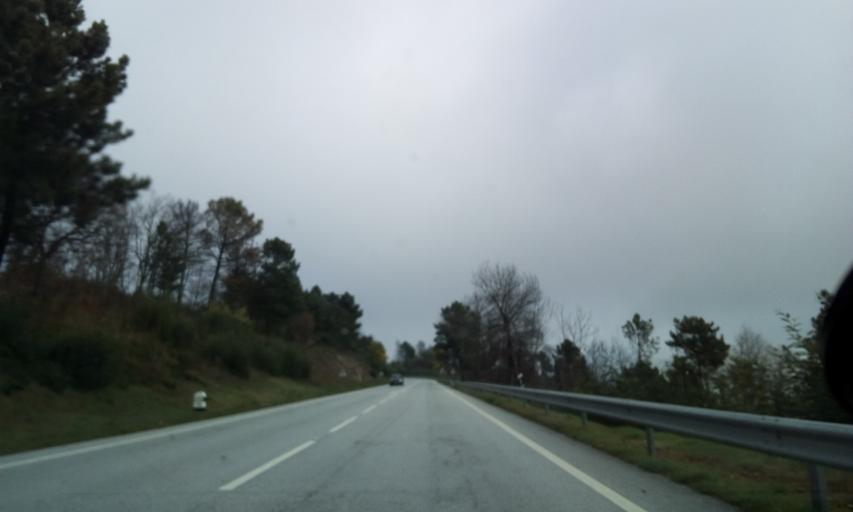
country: PT
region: Guarda
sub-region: Celorico da Beira
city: Celorico da Beira
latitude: 40.6882
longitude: -7.4686
